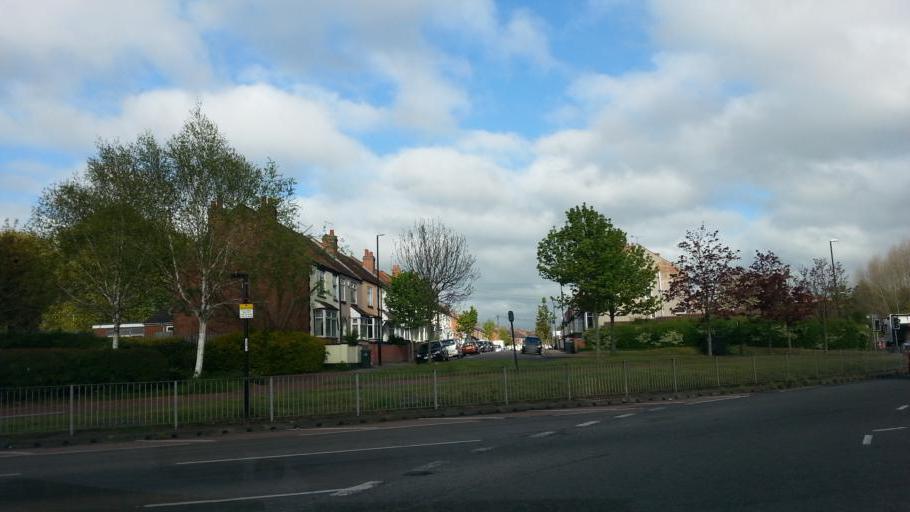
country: GB
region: England
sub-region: Warwickshire
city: Exhall
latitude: 52.4355
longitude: -1.4944
